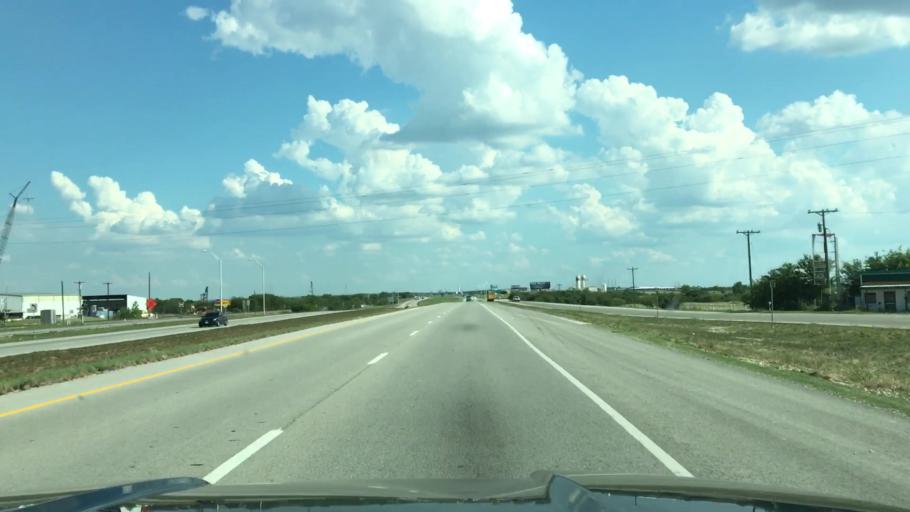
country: US
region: Texas
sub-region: Wise County
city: Decatur
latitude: 33.1983
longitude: -97.5628
